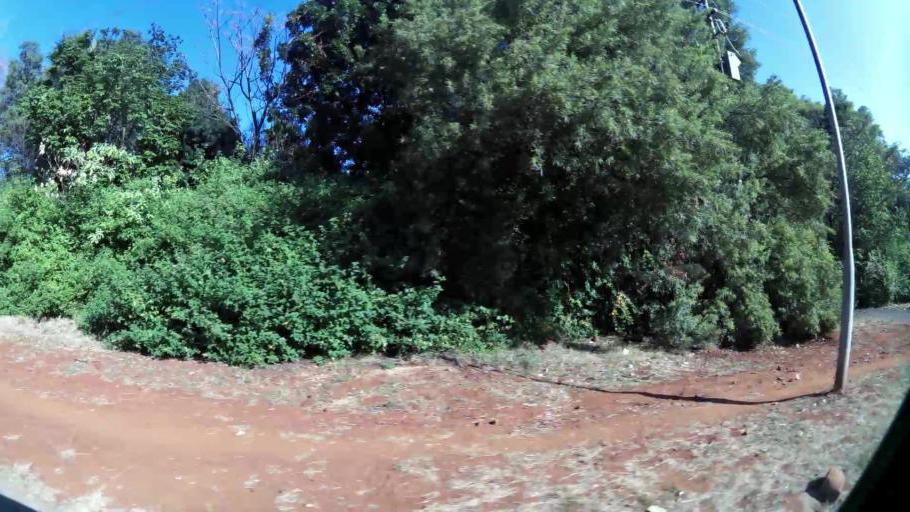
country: ZA
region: Gauteng
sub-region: City of Tshwane Metropolitan Municipality
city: Pretoria
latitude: -25.6815
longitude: 28.1341
